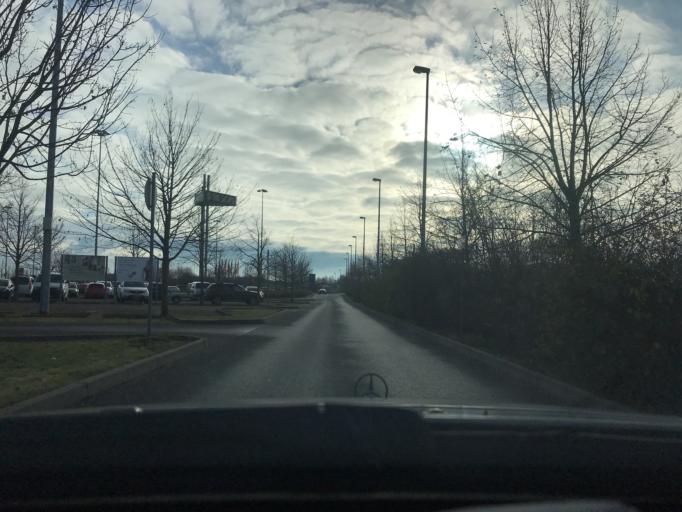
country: DE
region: Thuringia
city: Ingersleben
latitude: 50.9596
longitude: 10.9475
